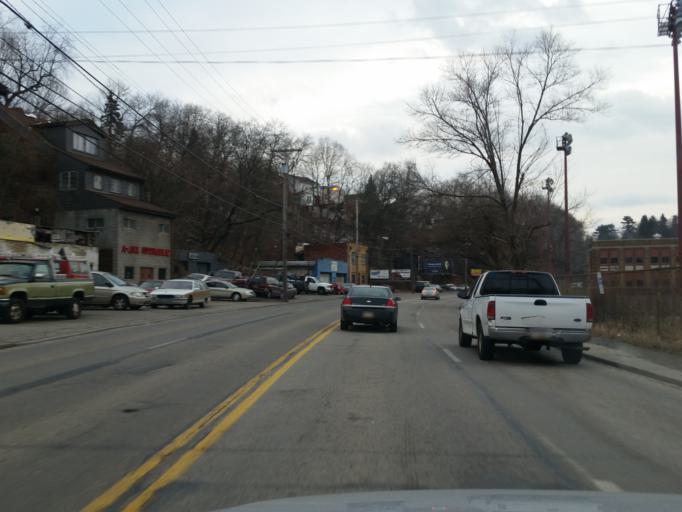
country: US
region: Pennsylvania
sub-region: Allegheny County
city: Mount Oliver
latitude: 40.3919
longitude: -79.9970
